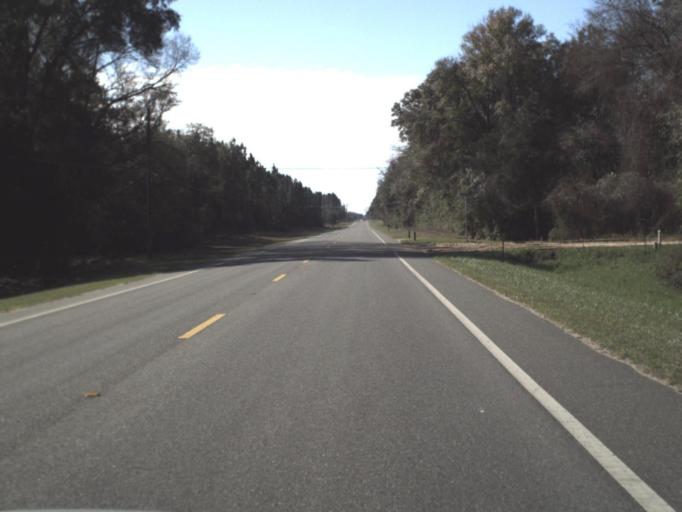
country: US
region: Florida
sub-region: Jackson County
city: Malone
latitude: 30.9179
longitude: -85.1608
